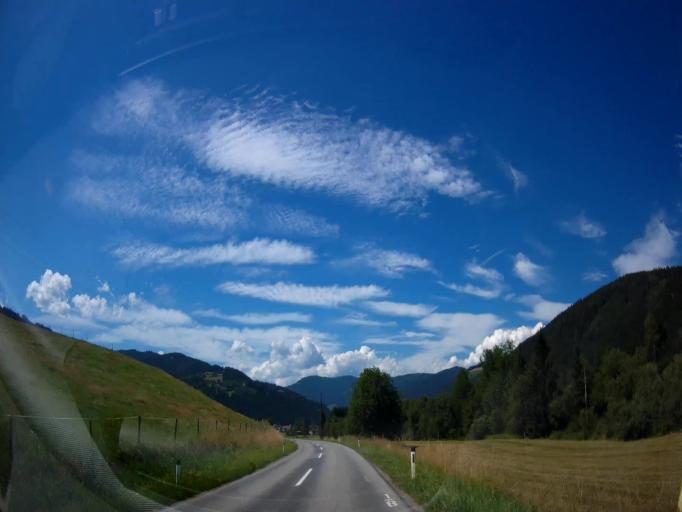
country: AT
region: Carinthia
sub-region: Politischer Bezirk Sankt Veit an der Glan
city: Glodnitz
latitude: 46.8659
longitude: 14.1248
